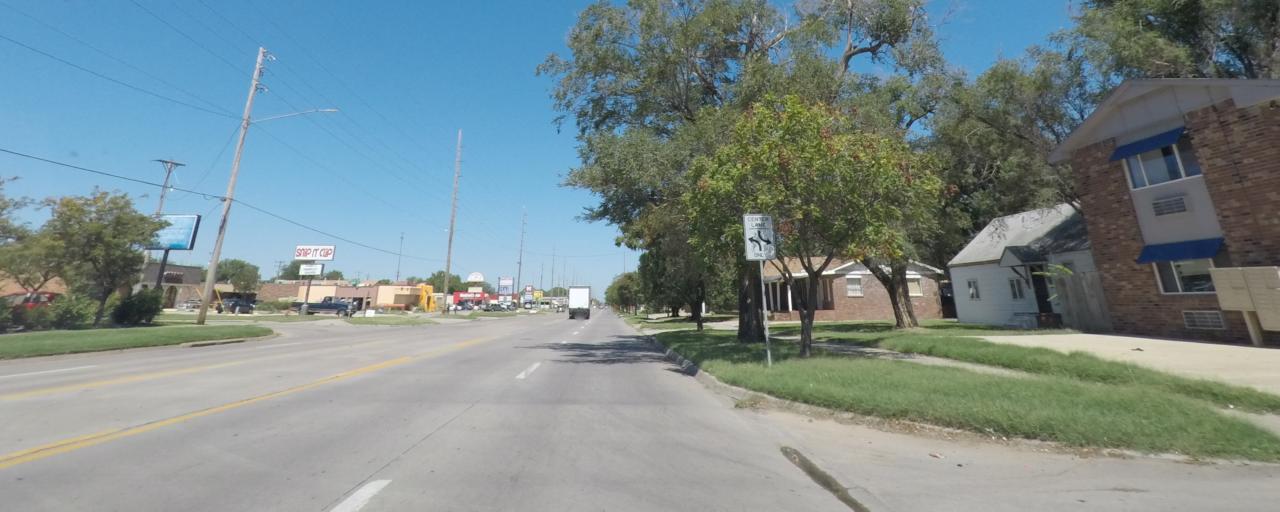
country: US
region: Kansas
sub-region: Sedgwick County
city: Wichita
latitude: 37.6561
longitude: -97.3527
